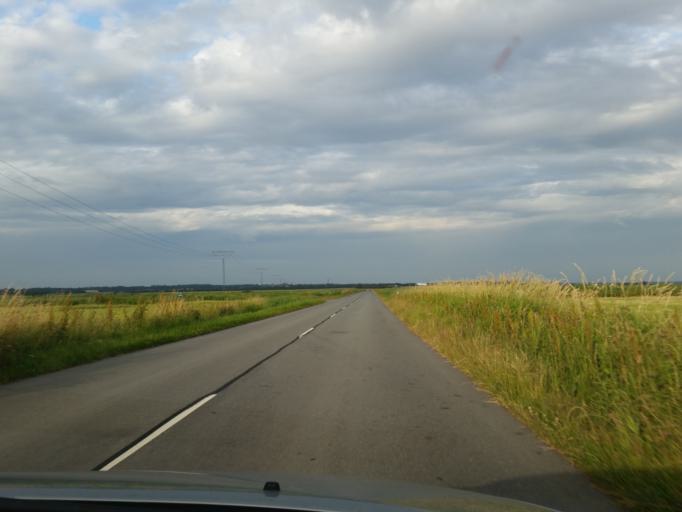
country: DK
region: South Denmark
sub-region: Tonder Kommune
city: Sherrebek
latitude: 55.1538
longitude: 8.7087
